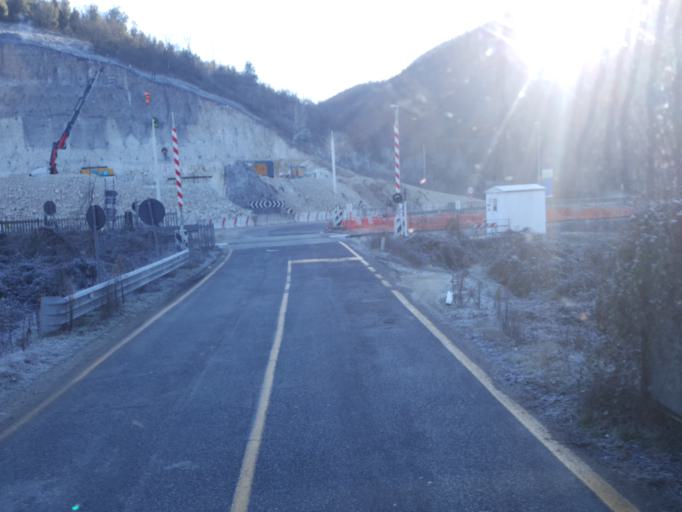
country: IT
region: Latium
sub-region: Provincia di Rieti
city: Colli sul Velino
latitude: 42.5058
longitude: 12.7456
